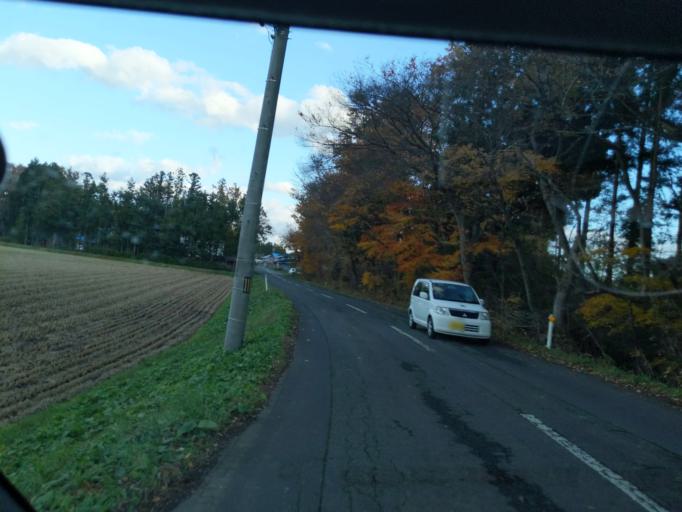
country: JP
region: Iwate
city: Mizusawa
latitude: 39.0776
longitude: 141.0442
